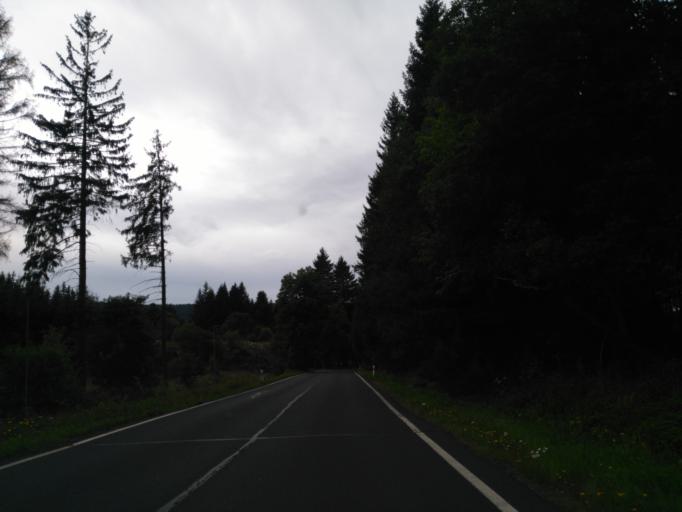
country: CZ
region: Karlovarsky
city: Abertamy
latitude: 50.3643
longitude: 12.7948
